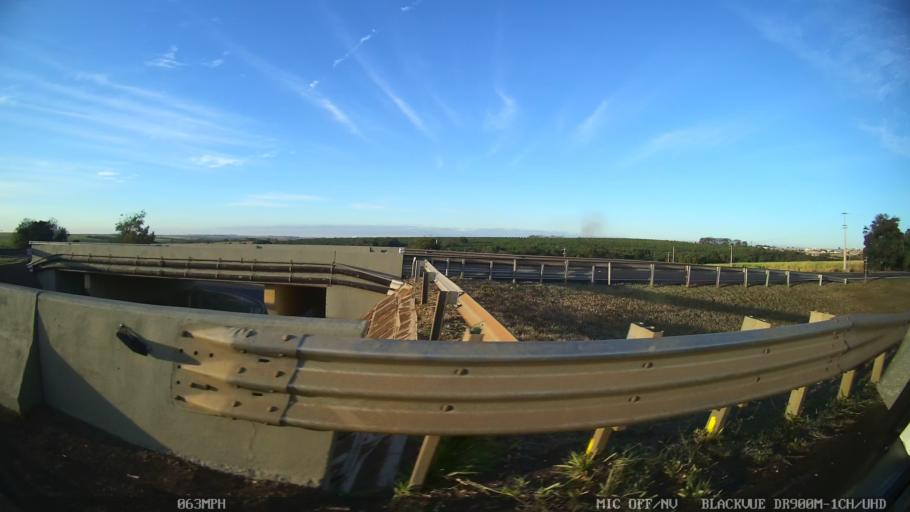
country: BR
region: Sao Paulo
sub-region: Catanduva
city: Catanduva
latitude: -21.1239
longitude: -49.0335
